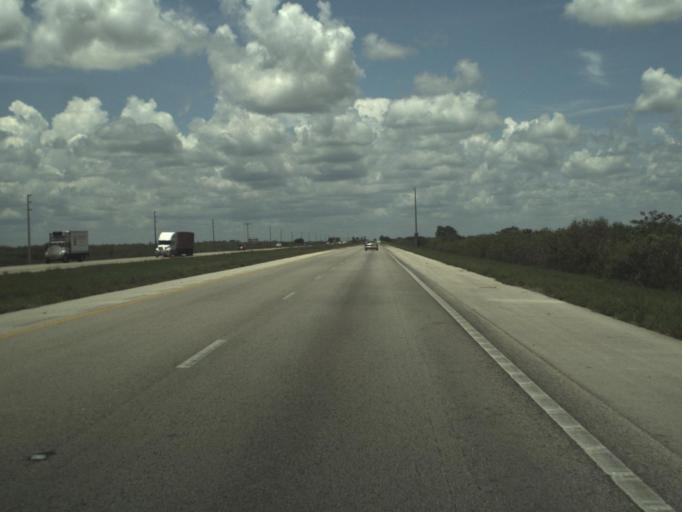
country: US
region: Florida
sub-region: Broward County
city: Weston
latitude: 26.1547
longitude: -80.7516
